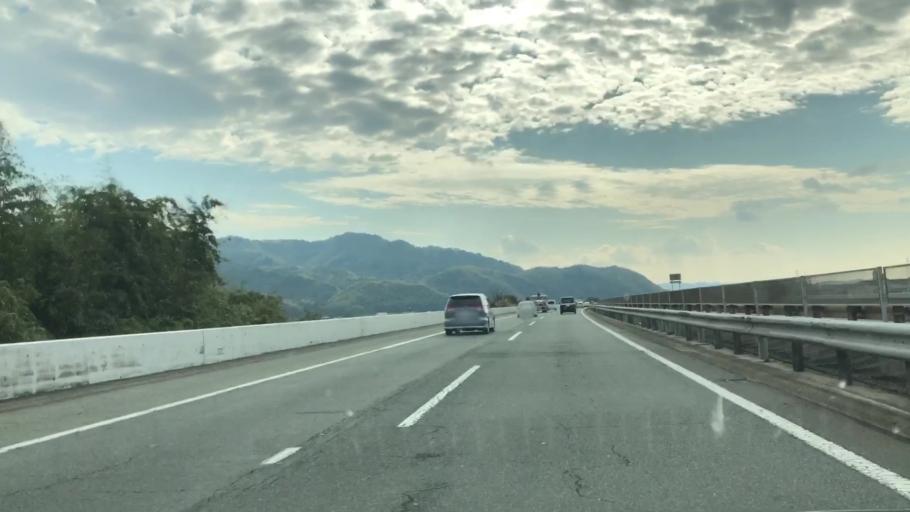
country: JP
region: Fukuoka
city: Setakamachi-takayanagi
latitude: 33.1812
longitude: 130.5181
